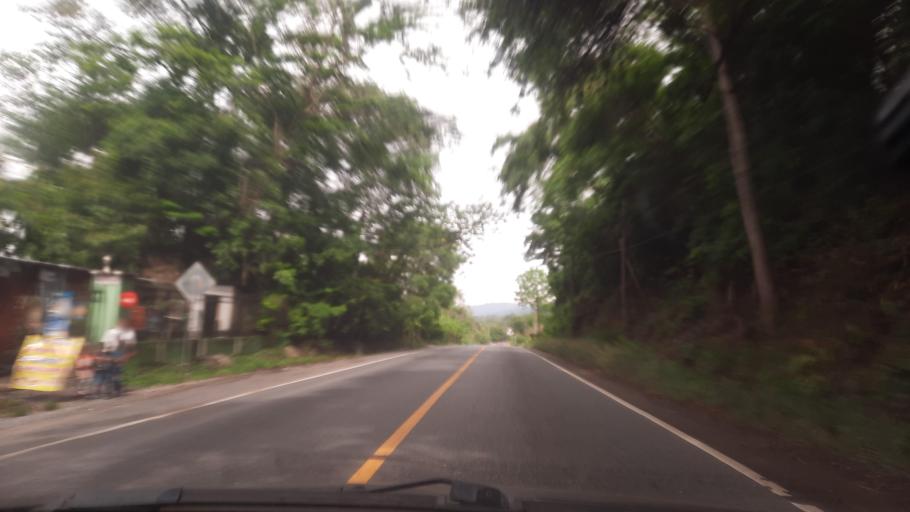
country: GT
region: Izabal
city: Morales
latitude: 15.5230
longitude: -88.7890
